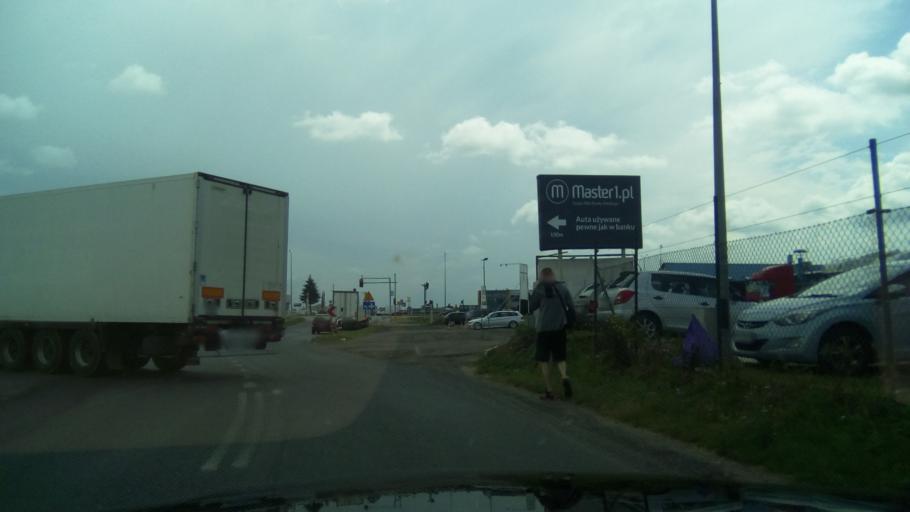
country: PL
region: Greater Poland Voivodeship
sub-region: Powiat poznanski
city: Komorniki
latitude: 52.3467
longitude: 16.8265
